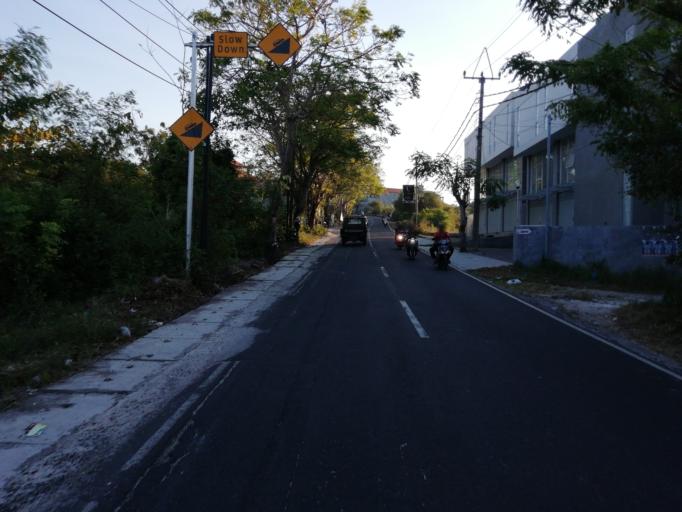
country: ID
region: Bali
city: Bualu
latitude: -8.8091
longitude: 115.1950
